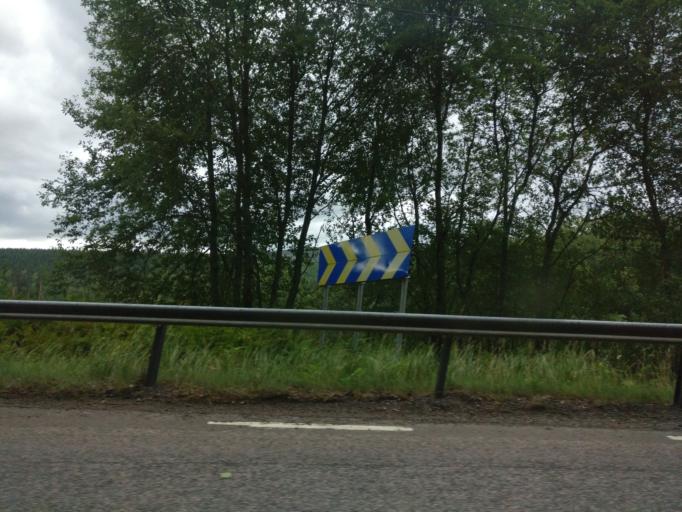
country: SE
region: Vaermland
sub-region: Torsby Kommun
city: Torsby
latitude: 60.6407
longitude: 13.0083
